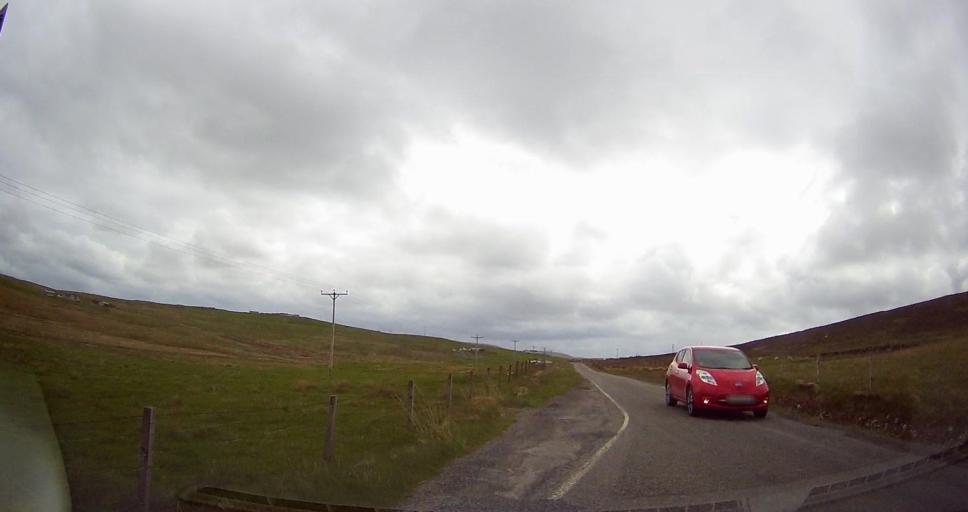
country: GB
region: Scotland
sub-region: Shetland Islands
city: Sandwick
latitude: 60.2476
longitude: -1.5097
